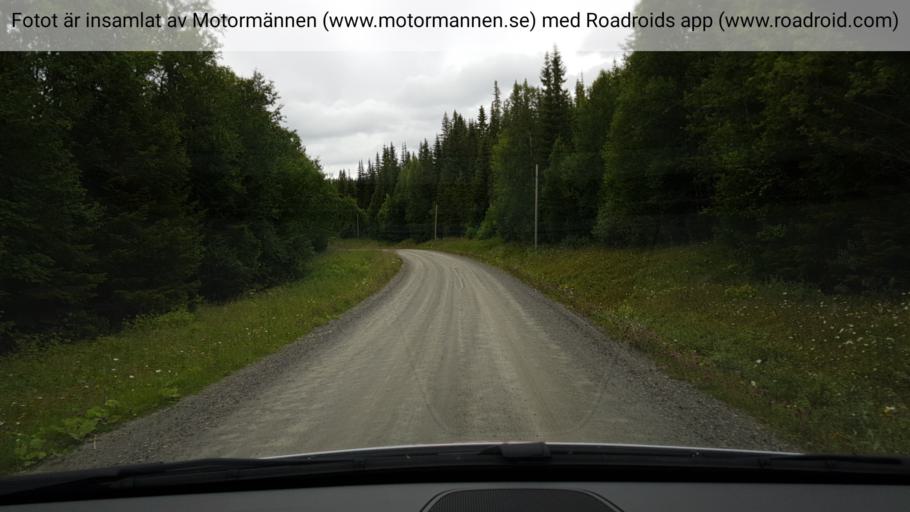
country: SE
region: Jaemtland
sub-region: Krokoms Kommun
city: Valla
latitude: 63.8424
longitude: 14.0647
